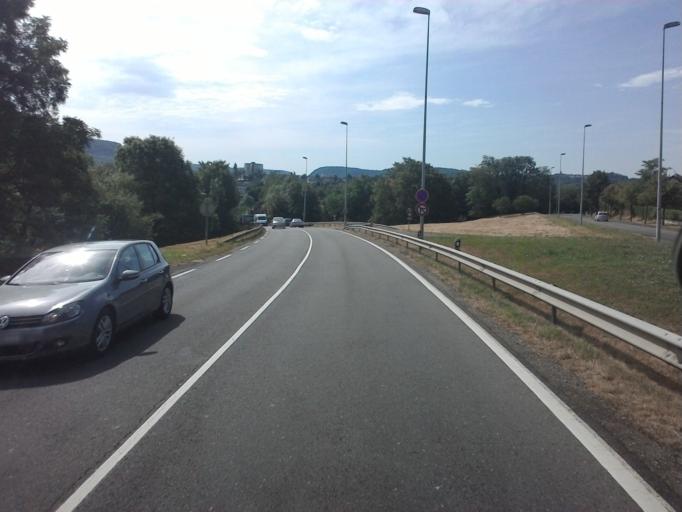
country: FR
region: Franche-Comte
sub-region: Departement du Jura
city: Lons-le-Saunier
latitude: 46.6885
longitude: 5.5621
